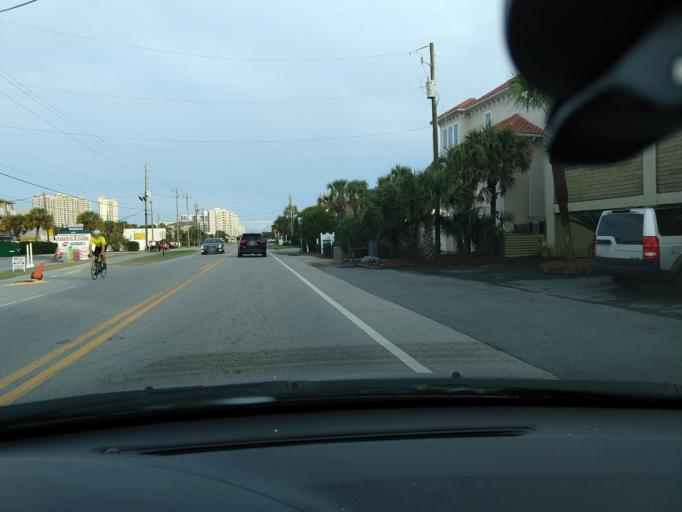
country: US
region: Florida
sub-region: Walton County
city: Miramar Beach
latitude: 30.3769
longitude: -86.3767
